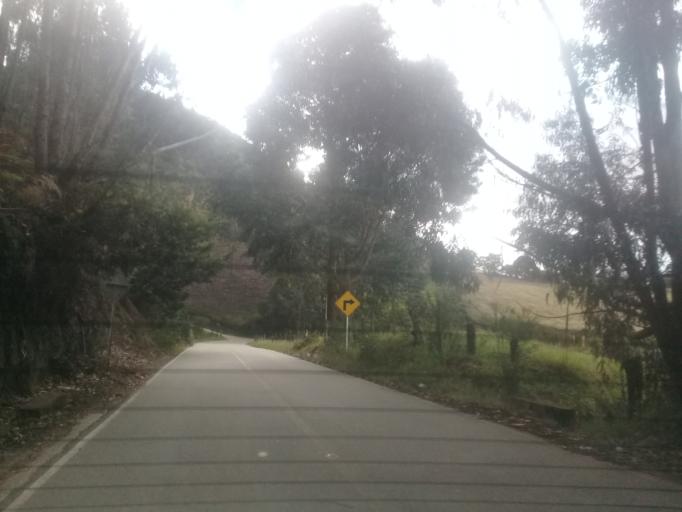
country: CO
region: Cundinamarca
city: Tabio
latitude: 4.9309
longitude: -74.1260
